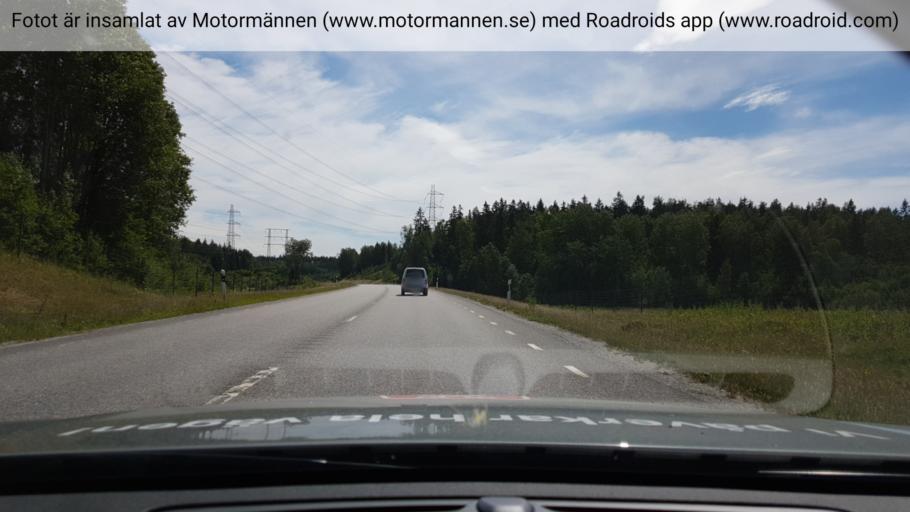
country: SE
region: Stockholm
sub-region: Sodertalje Kommun
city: Pershagen
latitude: 59.1766
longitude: 17.6905
